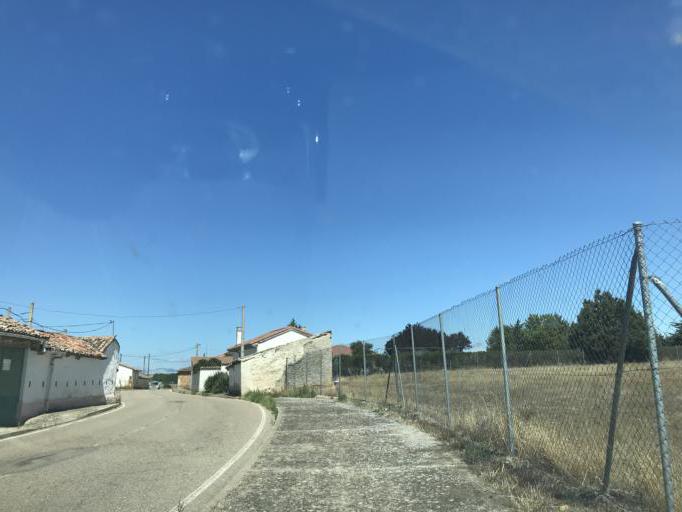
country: ES
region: Castille and Leon
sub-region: Provincia de Palencia
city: Herrera de Pisuerga
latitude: 42.6176
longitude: -4.3584
